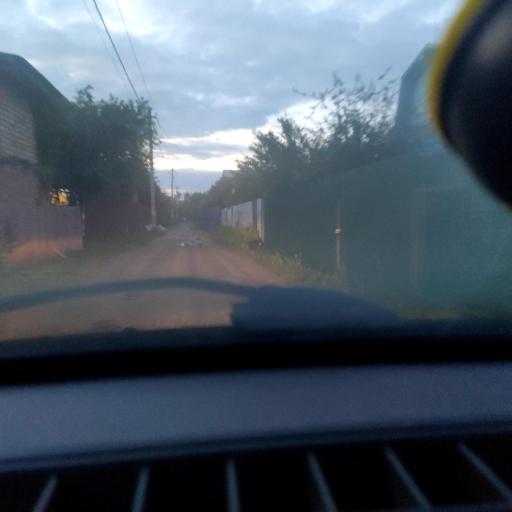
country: RU
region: Samara
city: Tol'yatti
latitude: 53.5949
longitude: 49.3148
